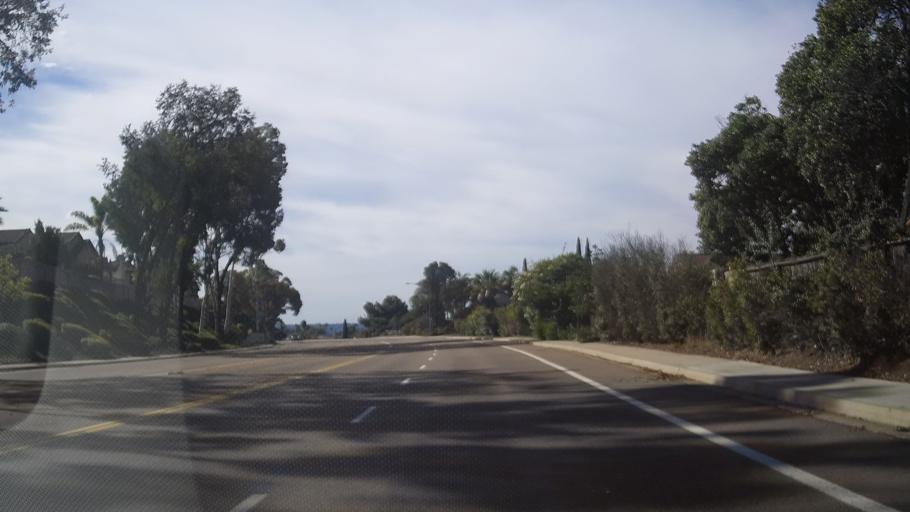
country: US
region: California
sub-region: San Diego County
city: Fairbanks Ranch
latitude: 32.9616
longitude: -117.1199
